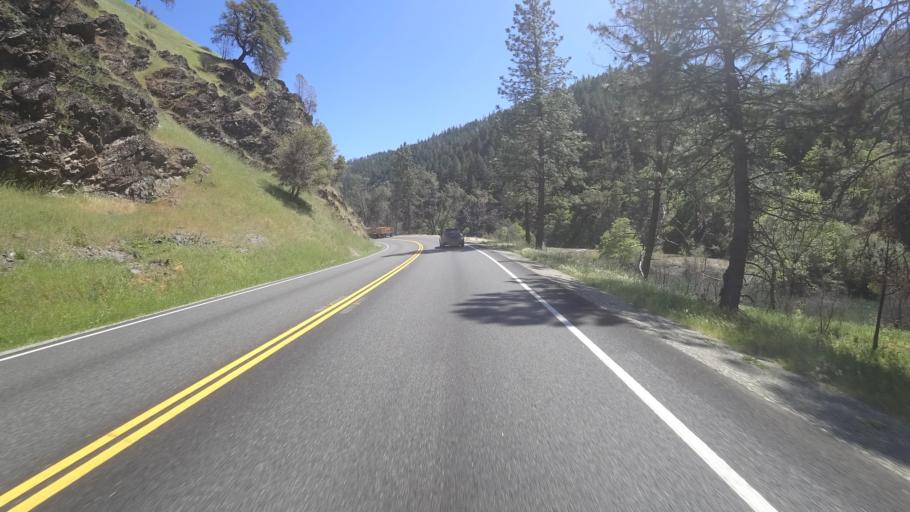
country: US
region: California
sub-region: Trinity County
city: Weaverville
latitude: 40.7683
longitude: -123.1214
